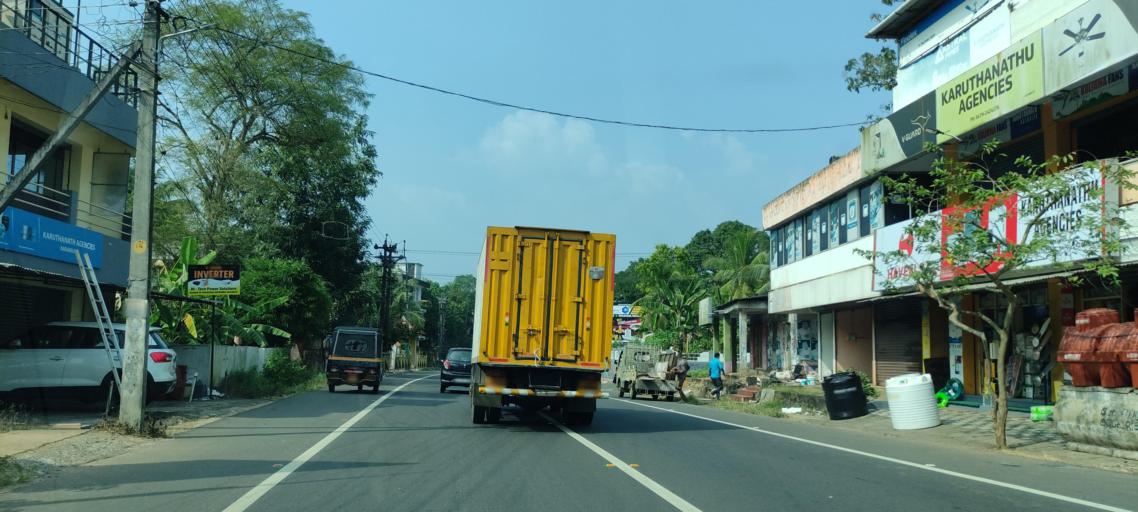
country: IN
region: Kerala
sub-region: Alappuzha
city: Chengannur
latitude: 9.2698
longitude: 76.6557
